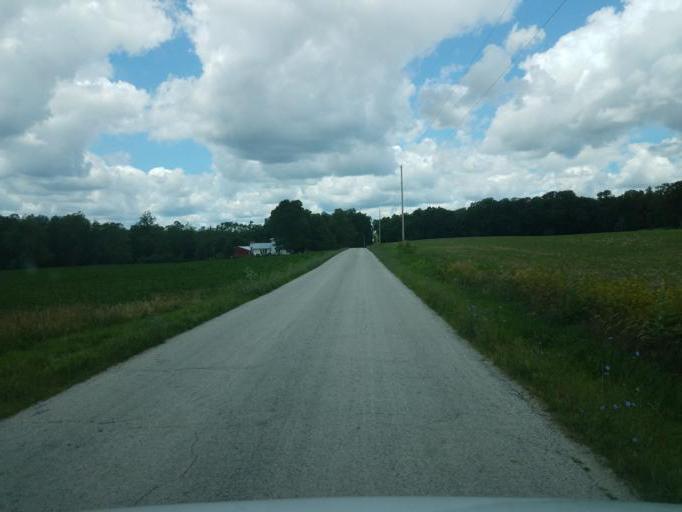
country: US
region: Ohio
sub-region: Richland County
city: Lexington
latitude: 40.6555
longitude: -82.6296
